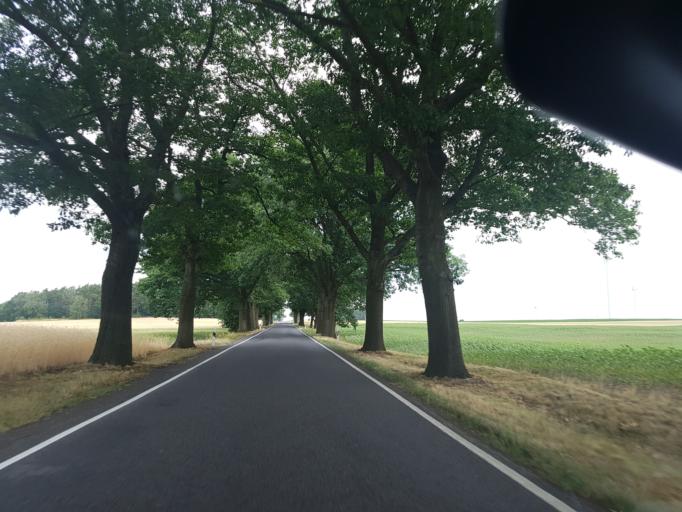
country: DE
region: Brandenburg
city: Hohenbucko
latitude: 51.6960
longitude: 13.5054
